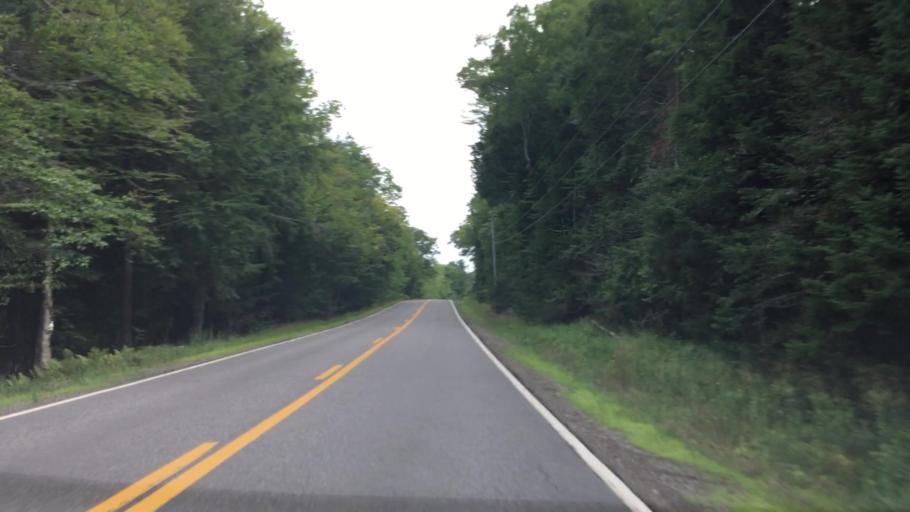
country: US
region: Maine
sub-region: Waldo County
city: Lincolnville
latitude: 44.3420
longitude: -69.0561
